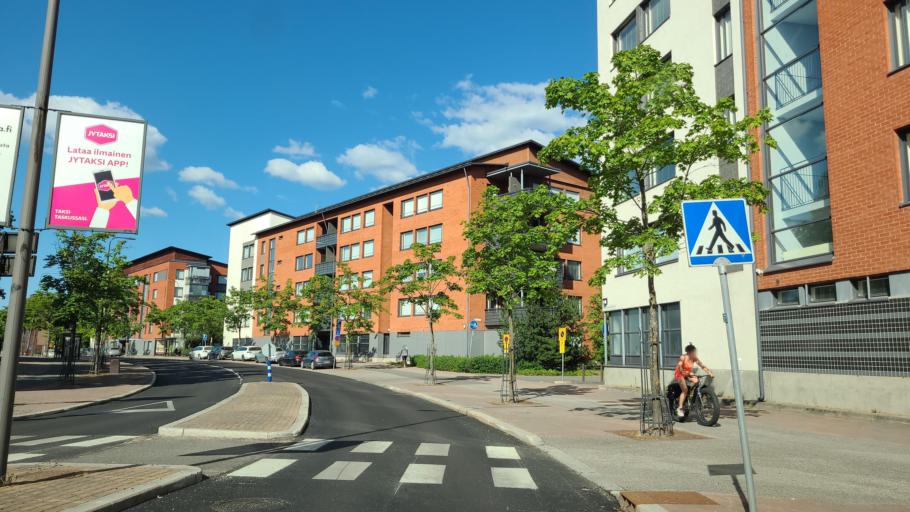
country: FI
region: Central Finland
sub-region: Jyvaeskylae
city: Jyvaeskylae
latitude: 62.2378
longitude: 25.7599
